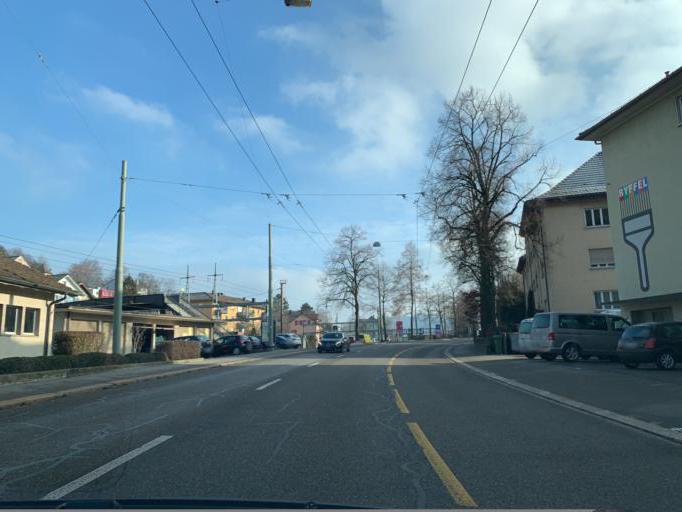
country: CH
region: Zurich
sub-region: Bezirk Winterthur
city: Mattenbach (Kreis 7) / Deutweg
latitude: 47.5011
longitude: 8.7421
